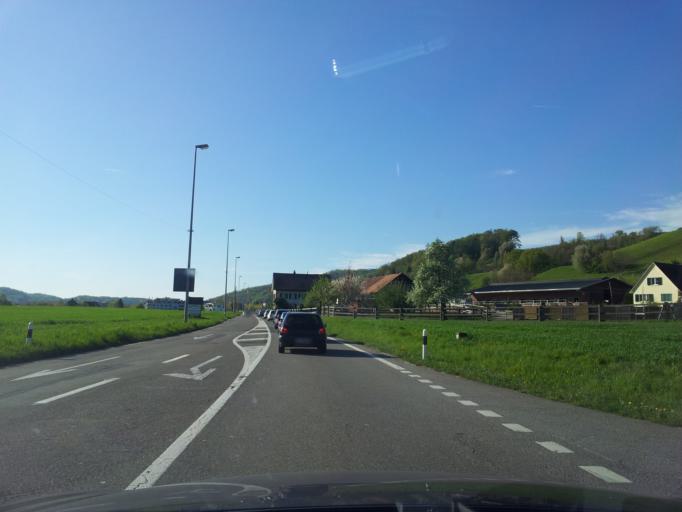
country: CH
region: Aargau
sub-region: Bezirk Baden
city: Neuenhof
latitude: 47.4565
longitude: 8.3459
